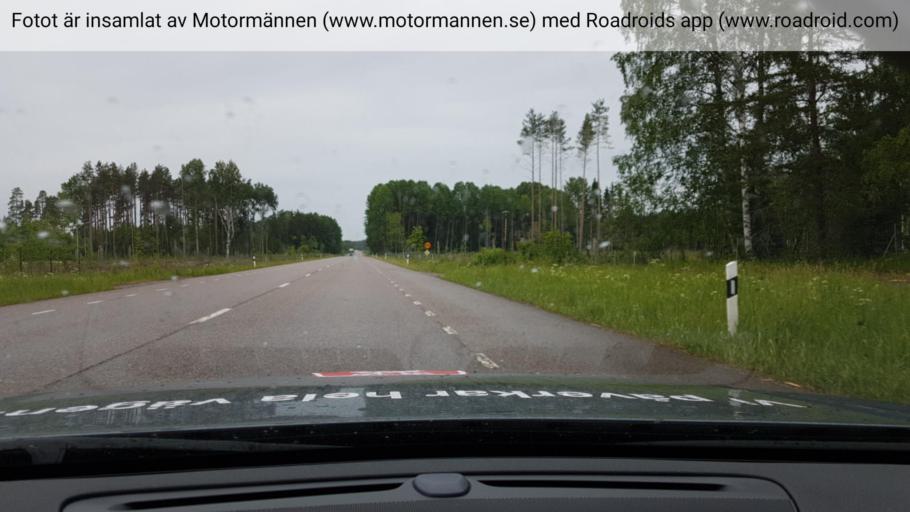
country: SE
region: Uppsala
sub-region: Alvkarleby Kommun
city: AElvkarleby
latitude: 60.5711
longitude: 17.4668
